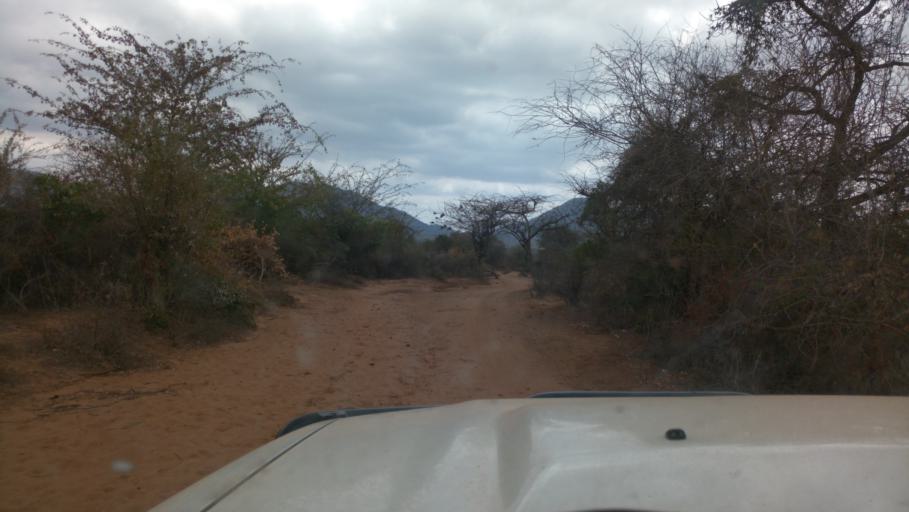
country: KE
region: Kitui
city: Kitui
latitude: -1.8531
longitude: 38.3625
